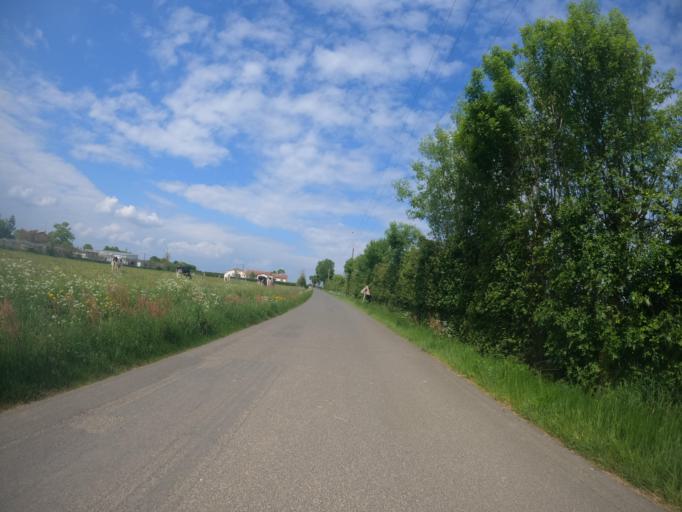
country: FR
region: Poitou-Charentes
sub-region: Departement des Deux-Sevres
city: Saint-Varent
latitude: 46.8921
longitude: -0.2888
